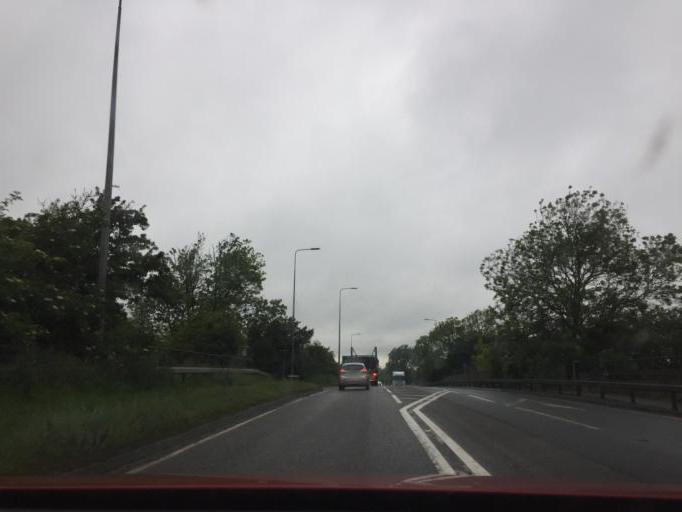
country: GB
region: England
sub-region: Leicestershire
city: Hinckley
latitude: 52.5273
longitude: -1.3940
